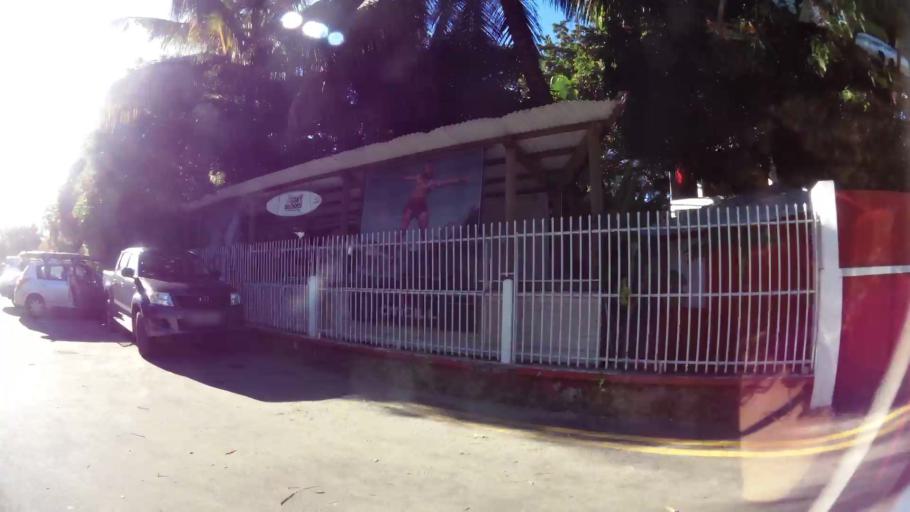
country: MU
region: Black River
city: Tamarin
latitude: -20.3273
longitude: 57.3772
